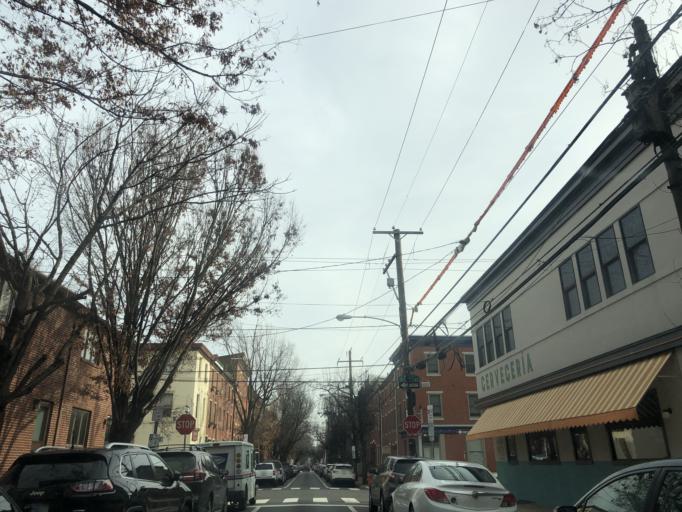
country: US
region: Pennsylvania
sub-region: Philadelphia County
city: Philadelphia
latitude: 39.9440
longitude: -75.1756
